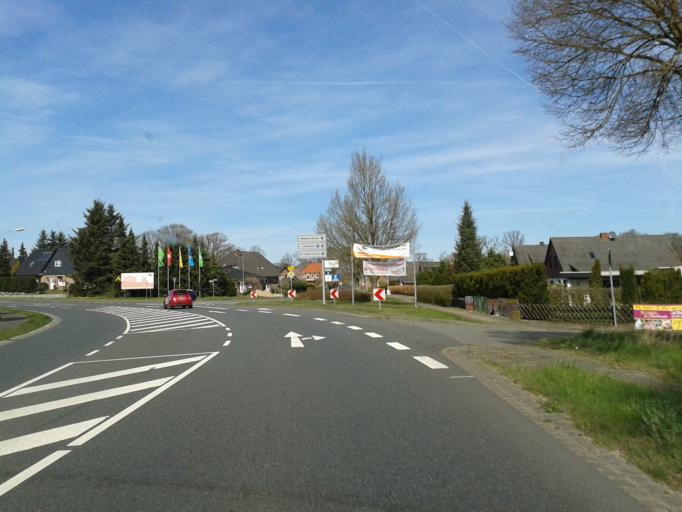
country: DE
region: Lower Saxony
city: Munster
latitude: 52.9803
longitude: 10.0951
